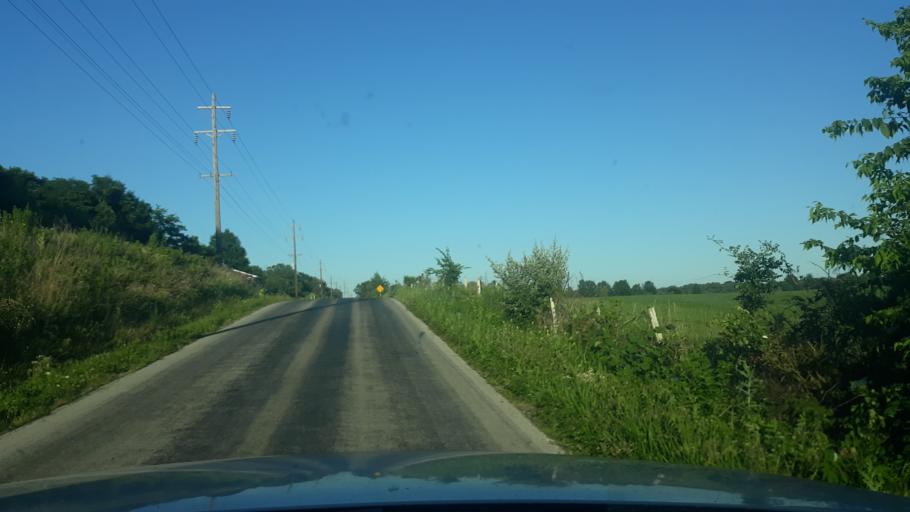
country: US
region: Illinois
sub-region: Saline County
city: Harrisburg
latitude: 37.8633
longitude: -88.6027
